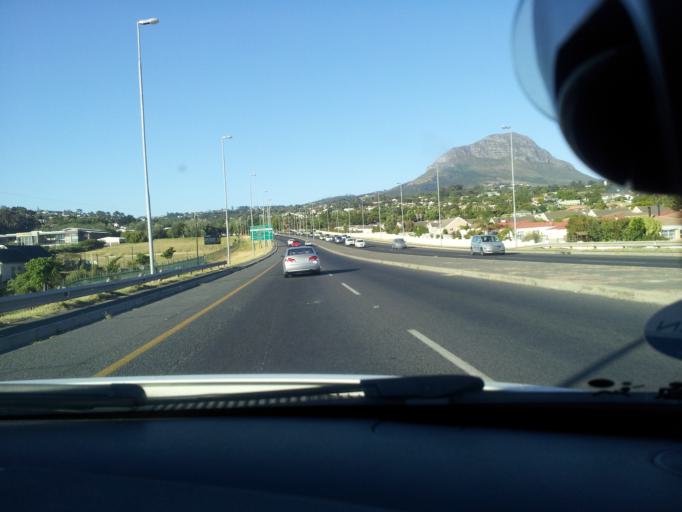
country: ZA
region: Western Cape
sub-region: Cape Winelands District Municipality
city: Stellenbosch
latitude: -34.0731
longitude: 18.8233
